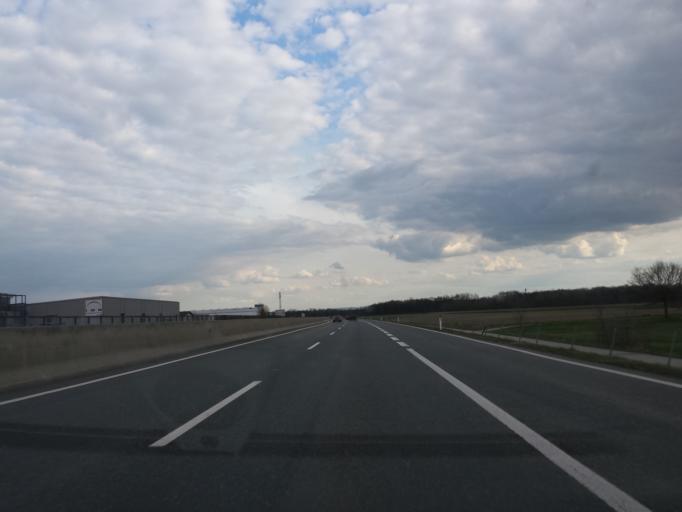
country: AT
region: Lower Austria
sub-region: Politischer Bezirk Tulln
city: Kirchberg am Wagram
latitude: 48.3905
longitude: 15.9181
